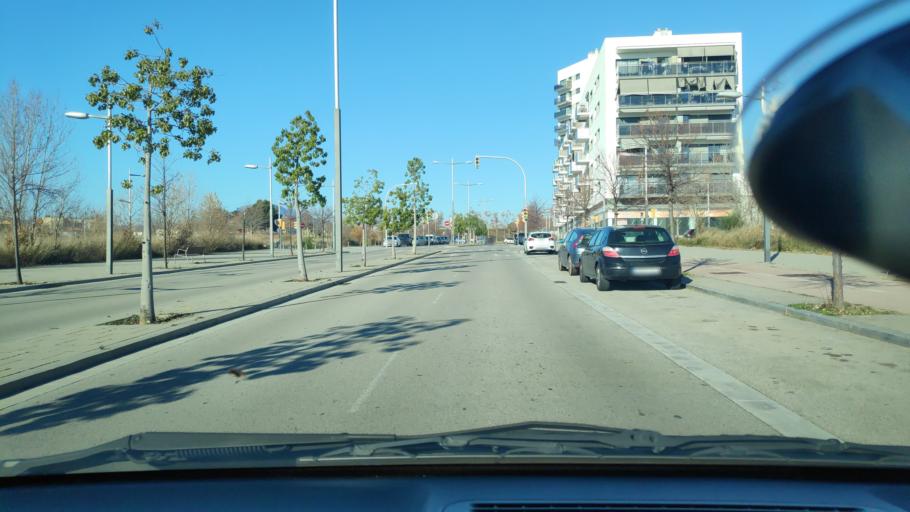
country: ES
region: Catalonia
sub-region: Provincia de Barcelona
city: Sant Quirze del Valles
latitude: 41.5484
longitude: 2.0790
